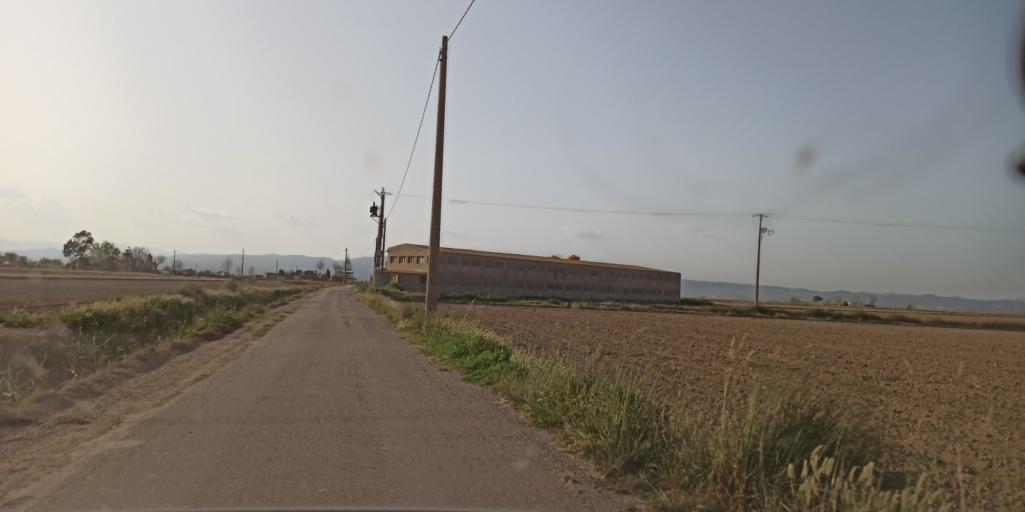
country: ES
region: Catalonia
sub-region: Provincia de Tarragona
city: Deltebre
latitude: 40.7531
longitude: 0.7570
